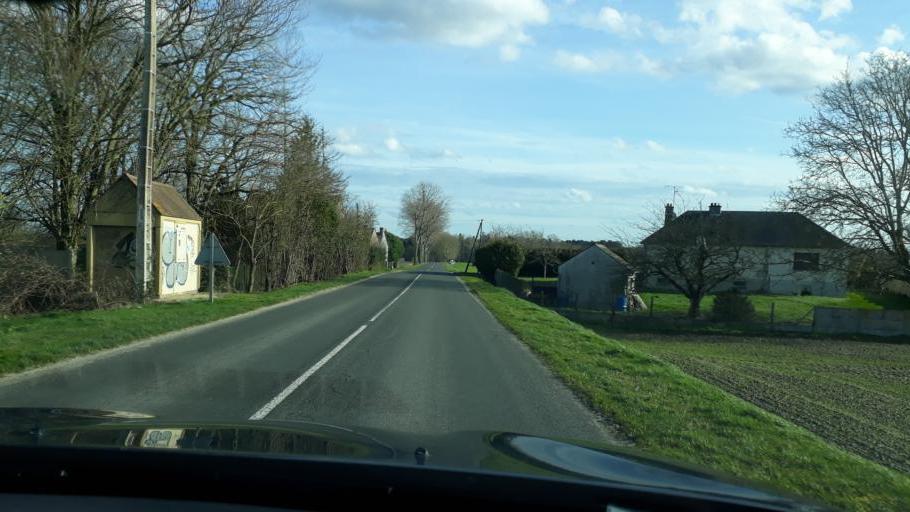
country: FR
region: Centre
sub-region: Departement du Loiret
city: Chilleurs-aux-Bois
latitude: 48.0663
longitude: 2.1474
